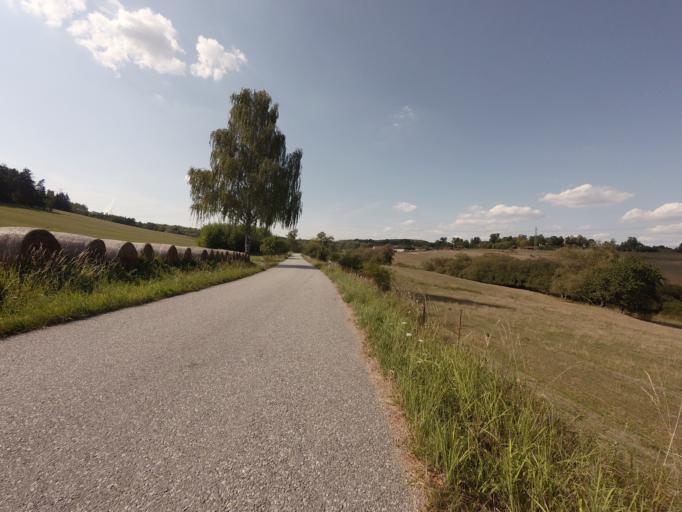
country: CZ
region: Jihocesky
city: Tyn nad Vltavou
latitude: 49.1693
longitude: 14.4250
